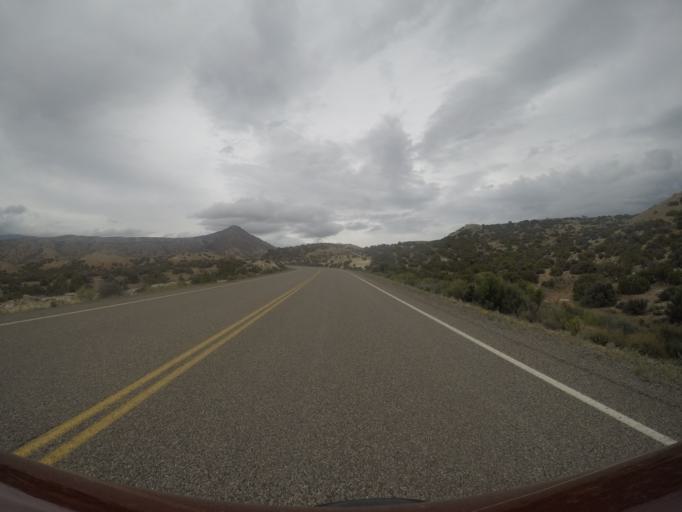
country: US
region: Wyoming
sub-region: Big Horn County
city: Lovell
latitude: 45.0068
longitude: -108.2684
